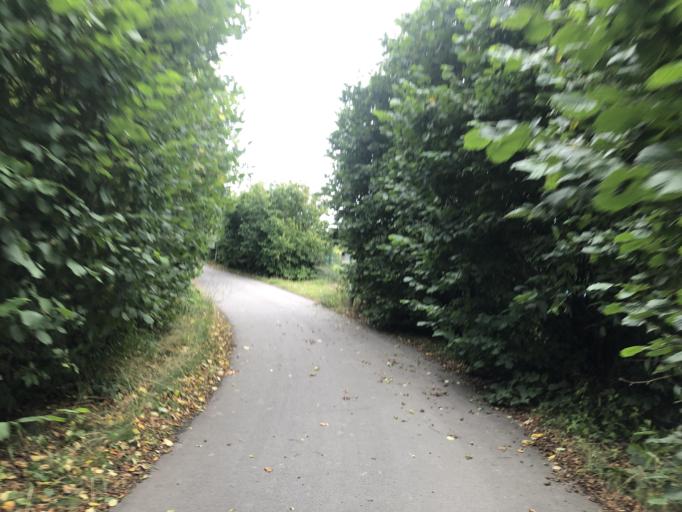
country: SE
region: Skane
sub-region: Burlovs Kommun
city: Arloev
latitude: 55.6075
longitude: 13.0700
